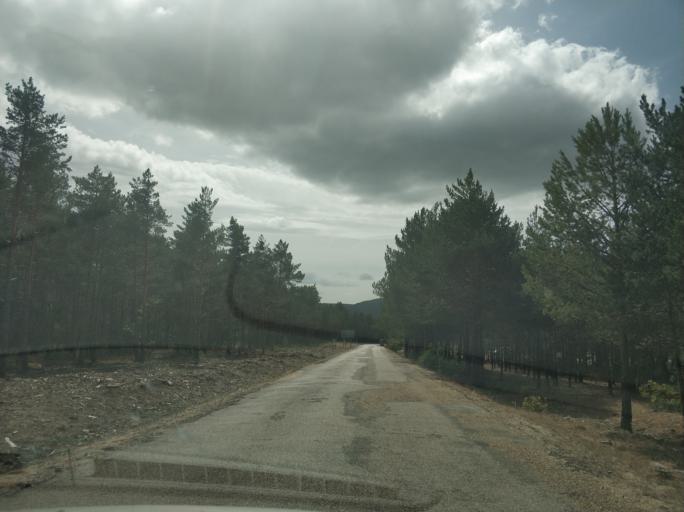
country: ES
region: Castille and Leon
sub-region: Provincia de Soria
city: Duruelo de la Sierra
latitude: 41.9571
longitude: -2.9199
